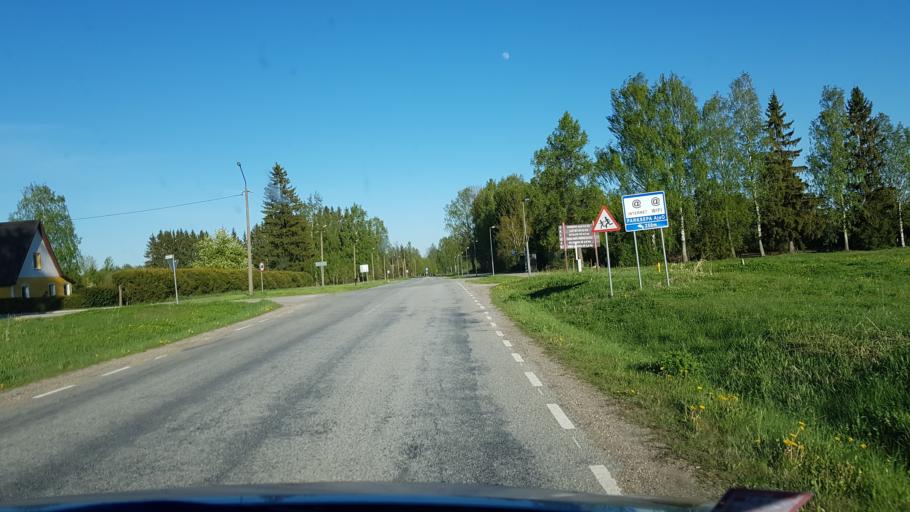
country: EE
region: Vorumaa
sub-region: Voru linn
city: Voru
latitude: 57.9055
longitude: 26.9832
